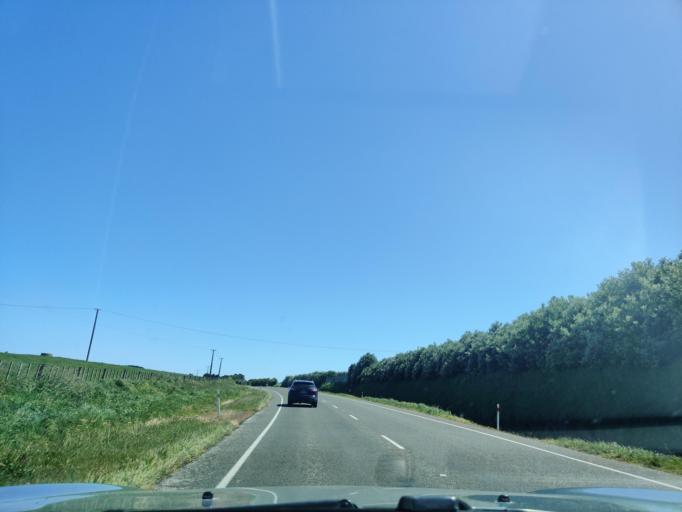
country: NZ
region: Taranaki
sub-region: South Taranaki District
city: Opunake
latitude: -39.5453
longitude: 174.0509
